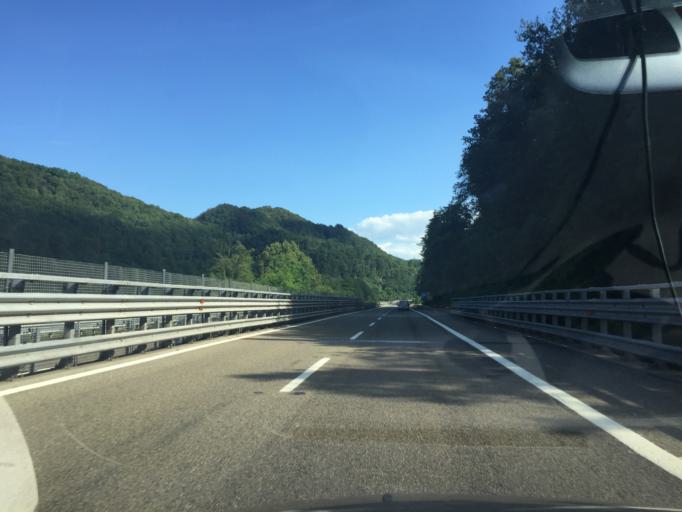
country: IT
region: Tuscany
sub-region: Provincia di Massa-Carrara
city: Villafranca in Lunigiana
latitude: 44.2783
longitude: 9.9497
